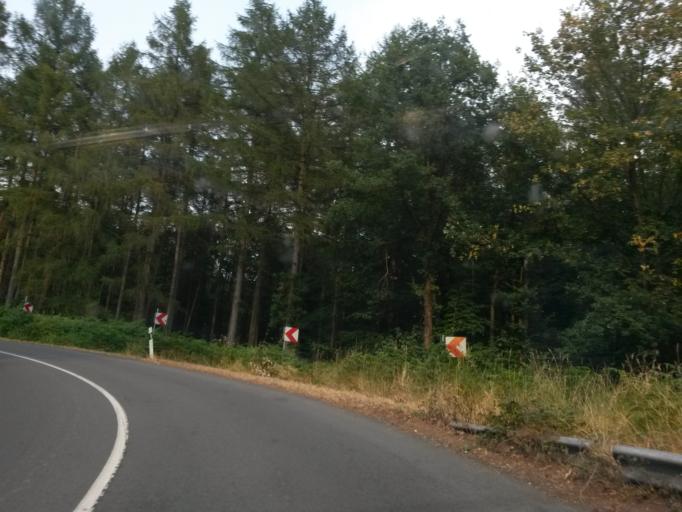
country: DE
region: North Rhine-Westphalia
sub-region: Regierungsbezirk Koln
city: Hennef
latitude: 50.7855
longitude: 7.3021
